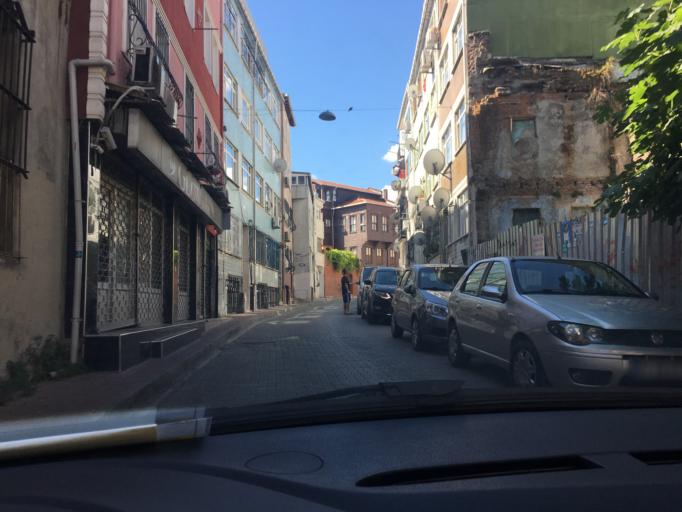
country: TR
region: Istanbul
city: Istanbul
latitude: 41.0204
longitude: 28.9556
